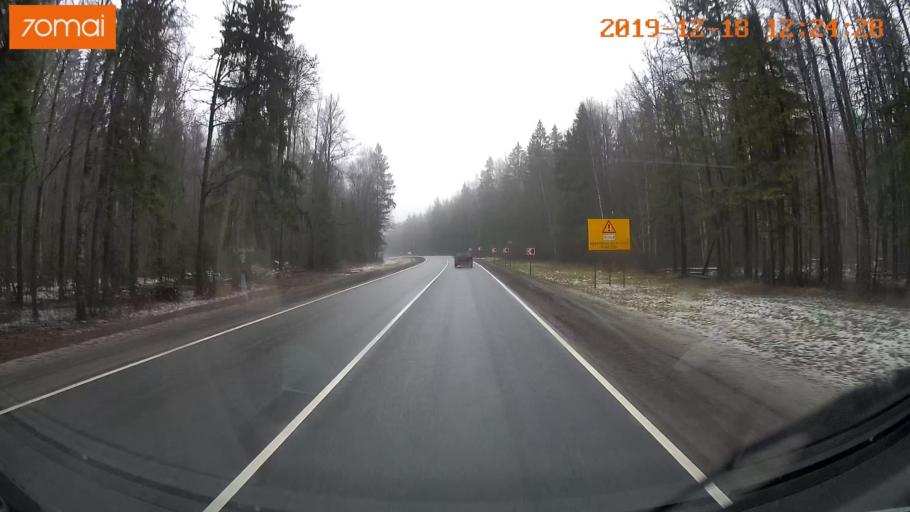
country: RU
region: Moskovskaya
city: Novopetrovskoye
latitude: 56.0251
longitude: 36.5006
